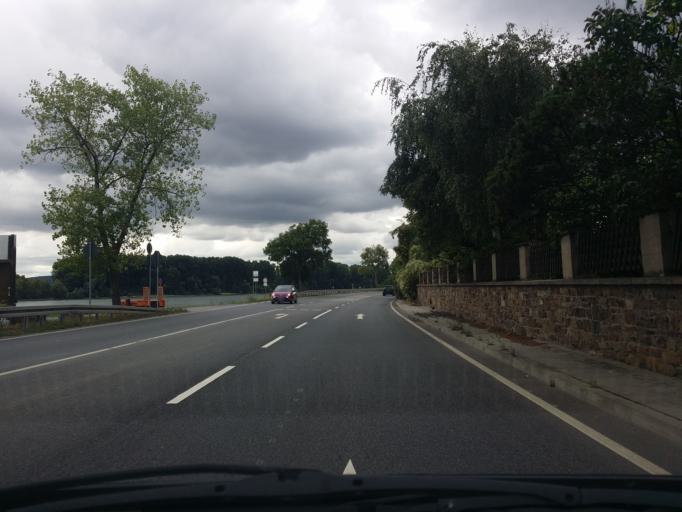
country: DE
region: Rheinland-Pfalz
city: Oestrich-Winkel
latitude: 49.9922
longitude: 8.0013
